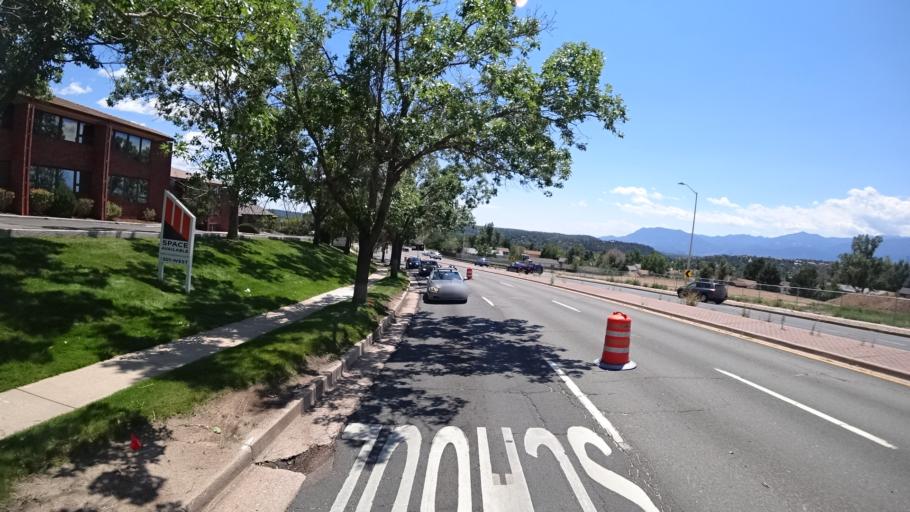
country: US
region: Colorado
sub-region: El Paso County
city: Colorado Springs
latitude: 38.9097
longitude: -104.7751
